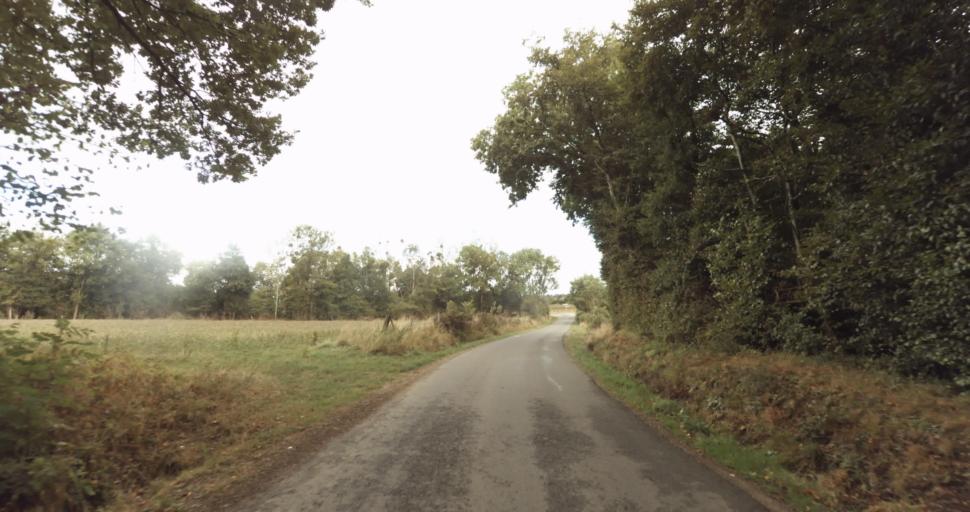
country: FR
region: Lower Normandy
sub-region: Departement de l'Orne
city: Vimoutiers
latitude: 48.8831
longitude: 0.2575
